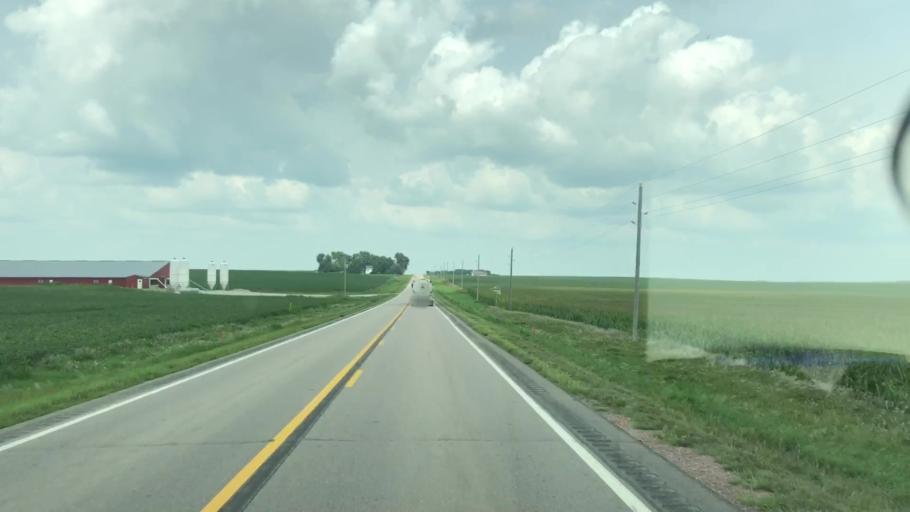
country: US
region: Iowa
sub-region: Plymouth County
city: Remsen
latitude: 42.7839
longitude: -95.9579
